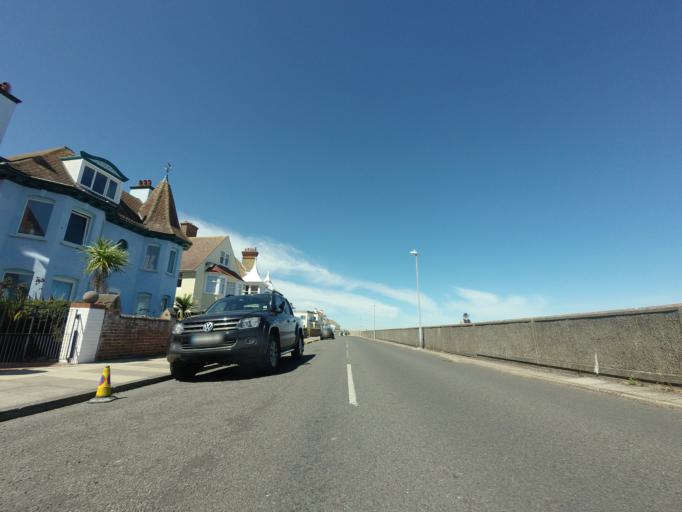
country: GB
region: England
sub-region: Kent
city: Deal
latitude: 51.2351
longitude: 1.4036
